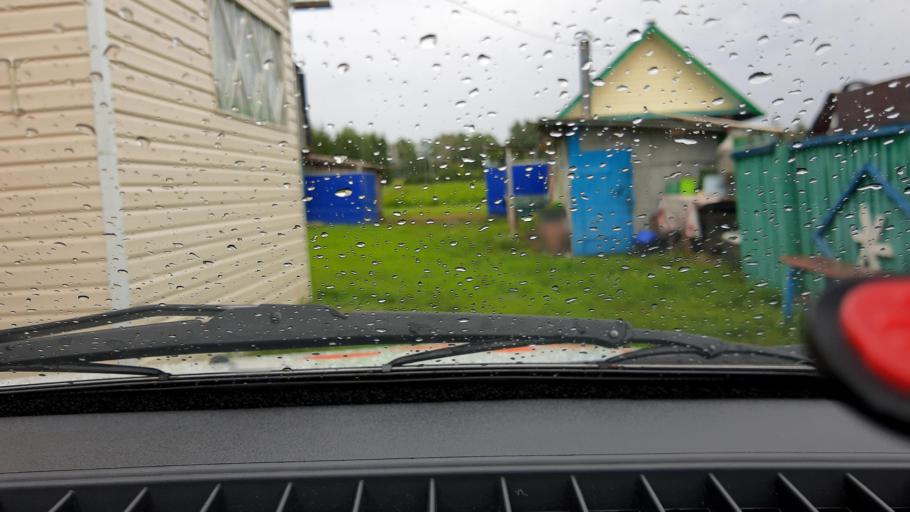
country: RU
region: Bashkortostan
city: Karmaskaly
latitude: 54.3778
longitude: 56.1126
